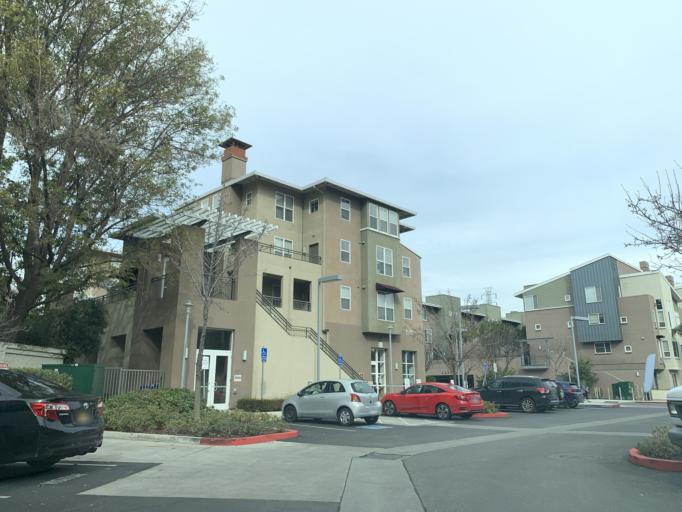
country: US
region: California
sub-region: Santa Clara County
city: Buena Vista
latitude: 37.3089
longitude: -121.9182
